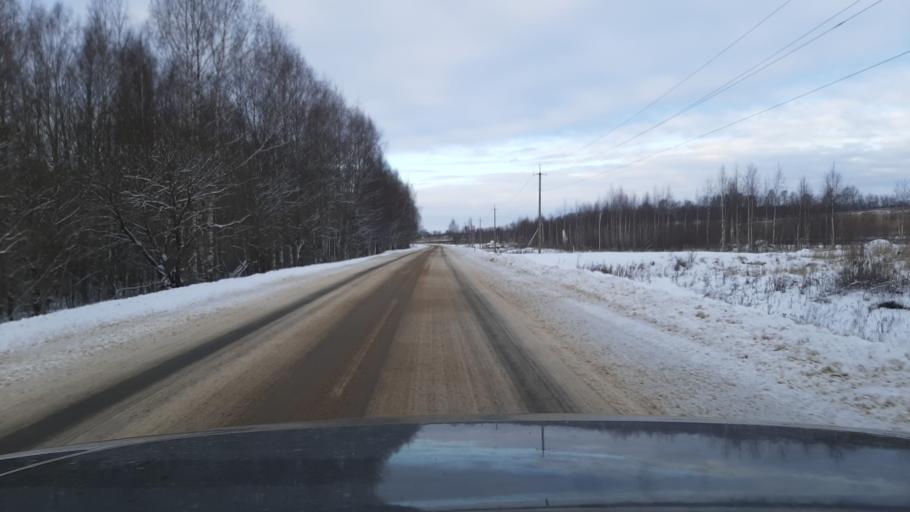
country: RU
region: Kostroma
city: Nerekhta
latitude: 57.4722
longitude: 40.6610
